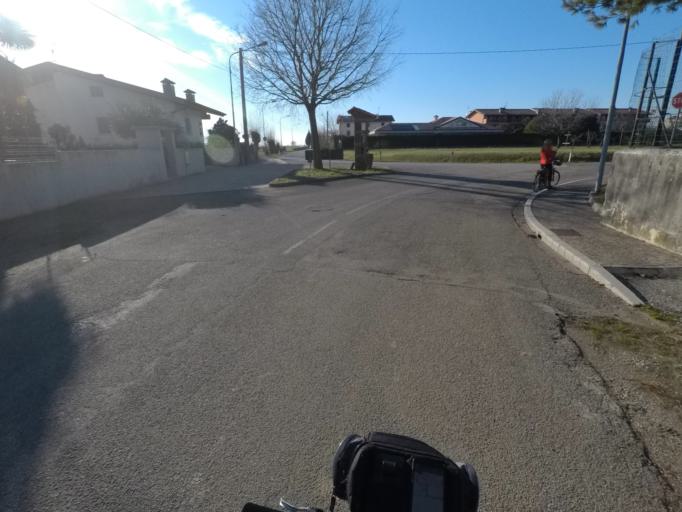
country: IT
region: Friuli Venezia Giulia
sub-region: Provincia di Udine
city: Povoletto
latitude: 46.1021
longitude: 13.3069
